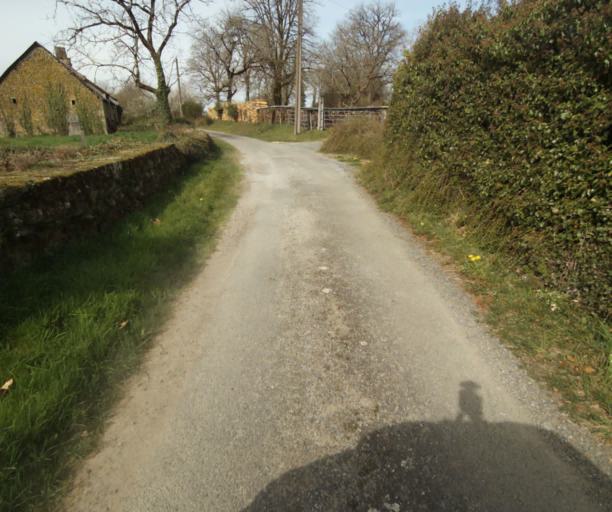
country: FR
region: Limousin
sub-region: Departement de la Correze
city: Correze
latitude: 45.4036
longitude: 1.8244
